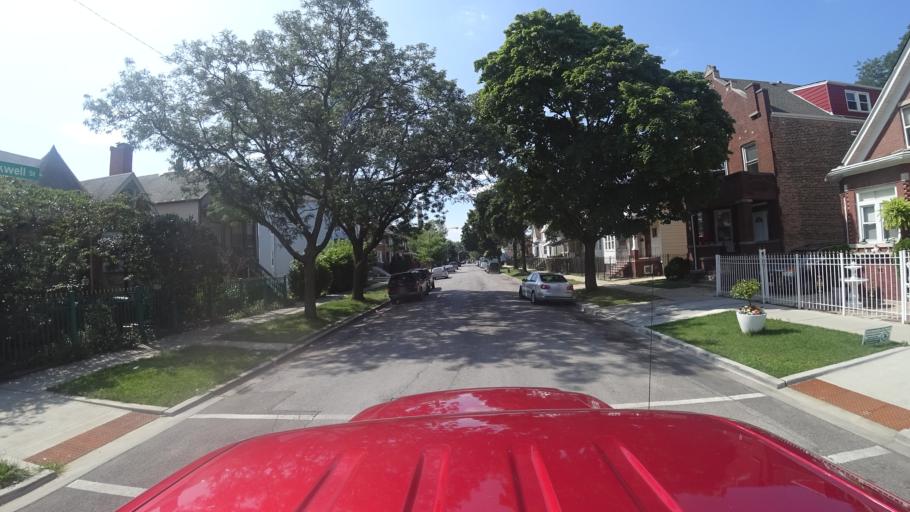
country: US
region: Illinois
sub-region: Cook County
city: Chicago
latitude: 41.7952
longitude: -87.6890
